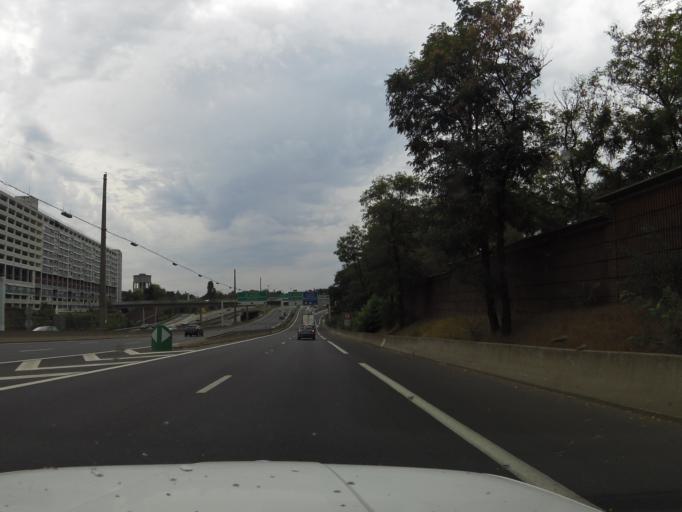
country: FR
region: Rhone-Alpes
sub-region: Departement du Rhone
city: Bron
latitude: 45.7320
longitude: 4.8995
